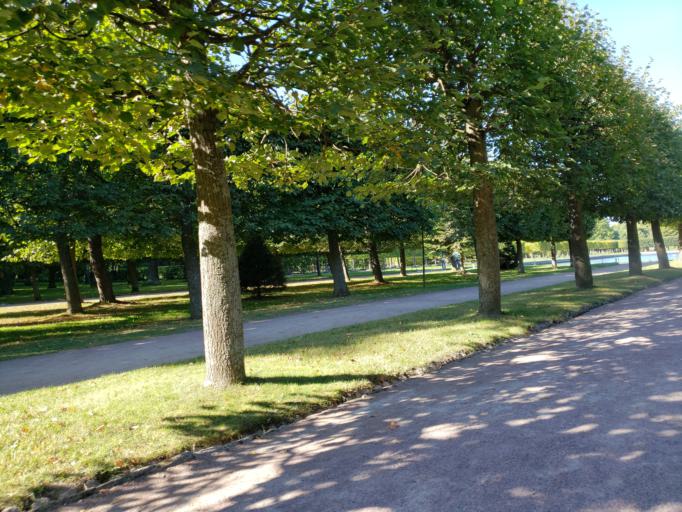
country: RU
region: St.-Petersburg
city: Peterhof
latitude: 59.8881
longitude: 29.9001
